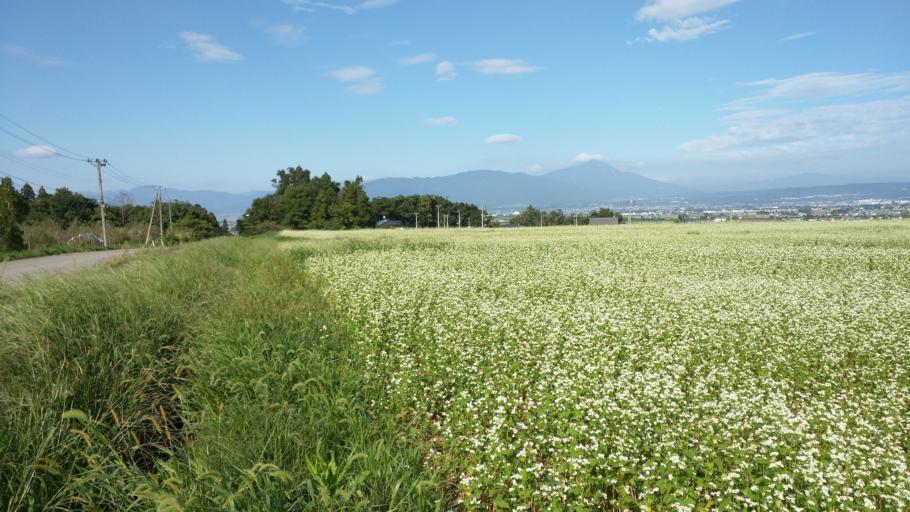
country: JP
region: Fukushima
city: Kitakata
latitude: 37.5118
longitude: 139.8175
